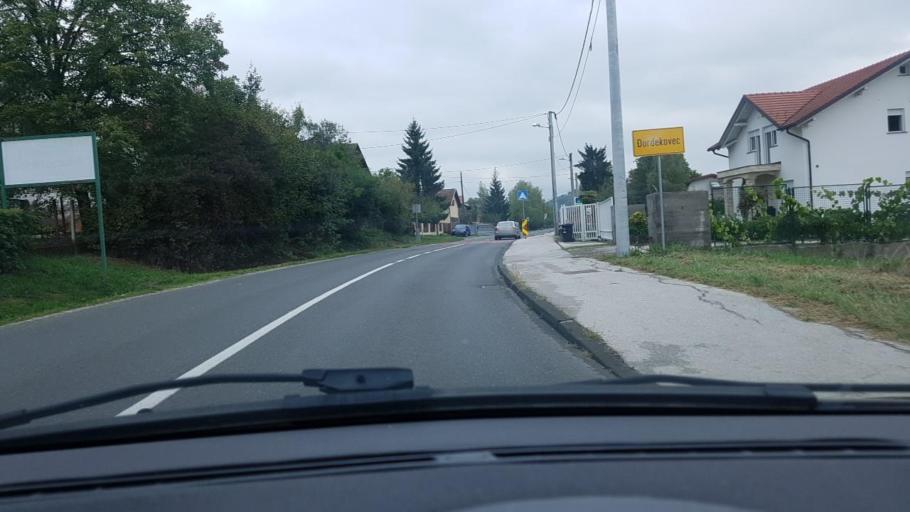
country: HR
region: Grad Zagreb
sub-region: Sesvete
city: Sesvete
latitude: 45.8721
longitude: 16.1128
